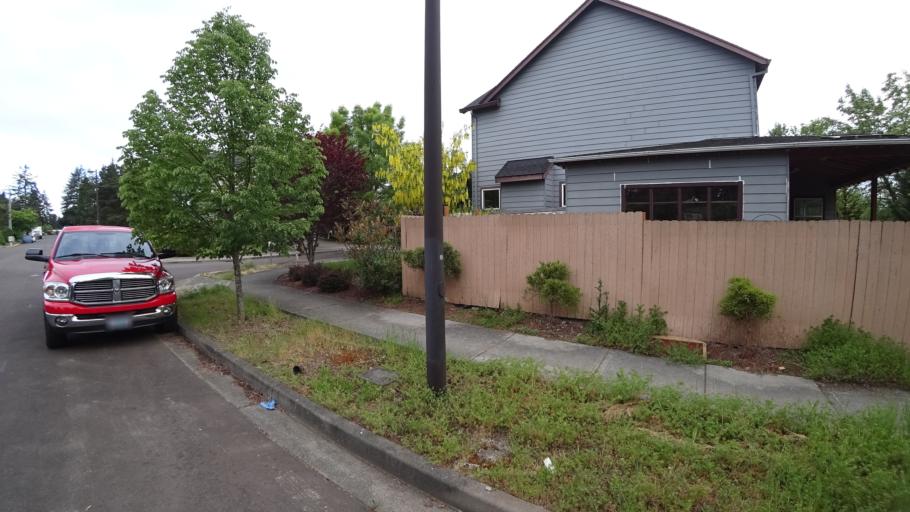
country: US
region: Oregon
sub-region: Washington County
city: Beaverton
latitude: 45.4783
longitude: -122.8147
